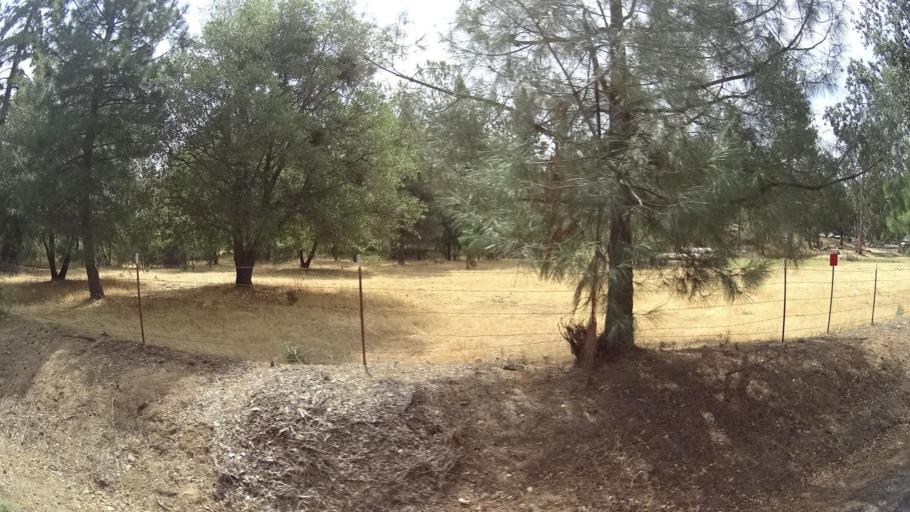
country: US
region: California
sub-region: Mariposa County
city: Midpines
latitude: 37.5079
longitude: -119.8444
